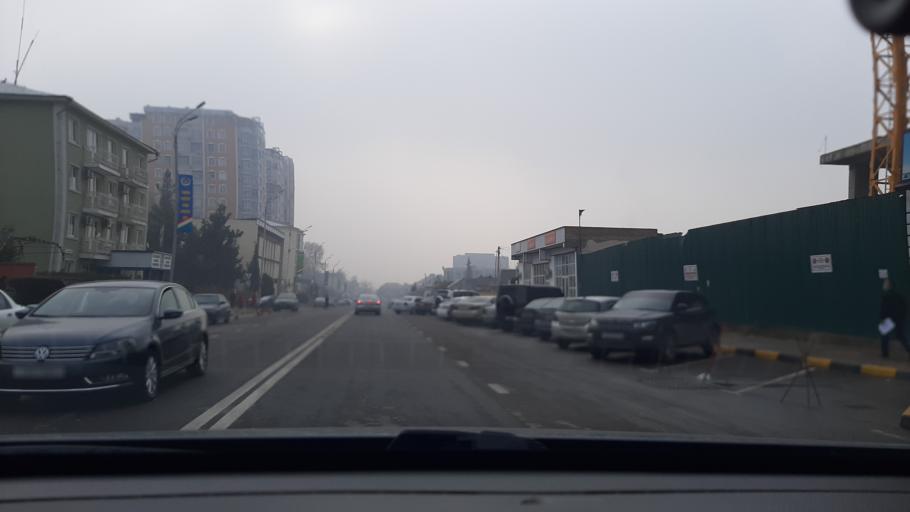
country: TJ
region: Dushanbe
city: Dushanbe
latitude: 38.5622
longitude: 68.7946
